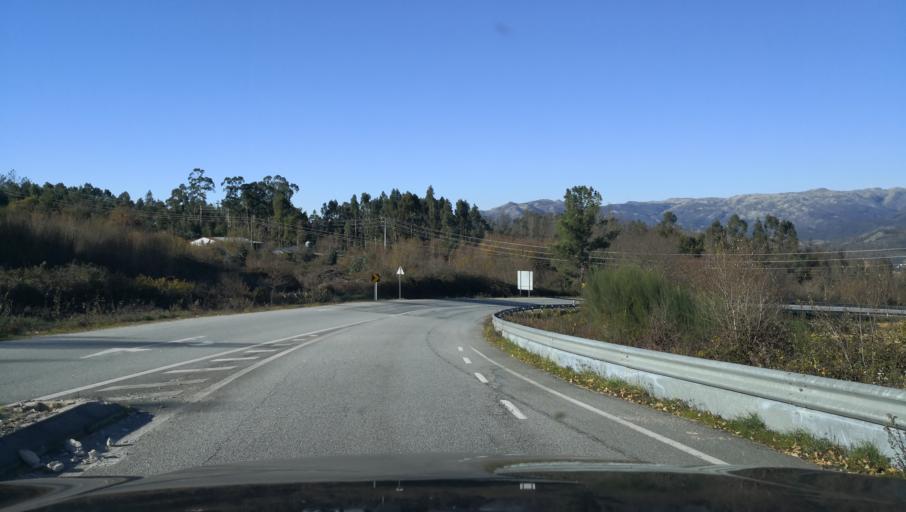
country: PT
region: Viseu
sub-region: Vouzela
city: Vouzela
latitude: 40.7219
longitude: -8.1326
